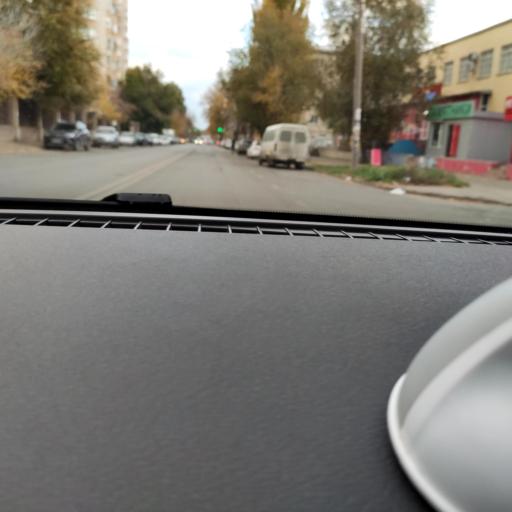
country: RU
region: Samara
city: Petra-Dubrava
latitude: 53.2322
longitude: 50.2761
